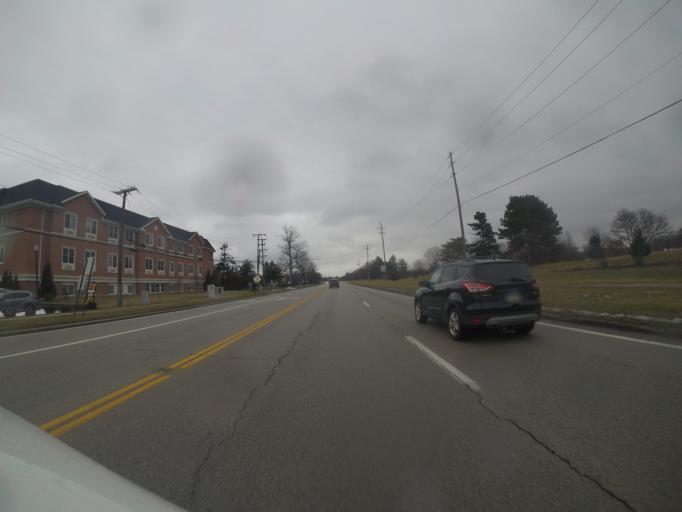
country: US
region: Ohio
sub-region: Wood County
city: Perrysburg
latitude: 41.5616
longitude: -83.6158
